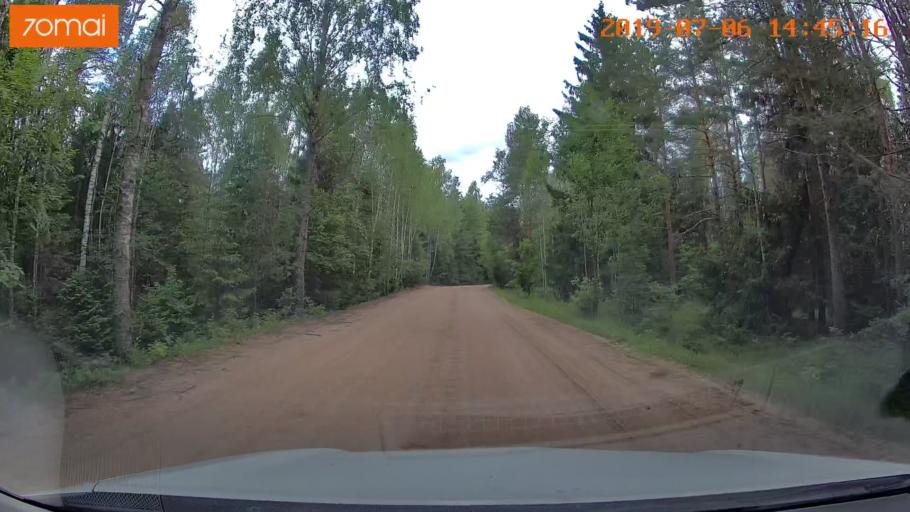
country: BY
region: Minsk
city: Ivyanyets
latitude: 53.9704
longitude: 26.6881
